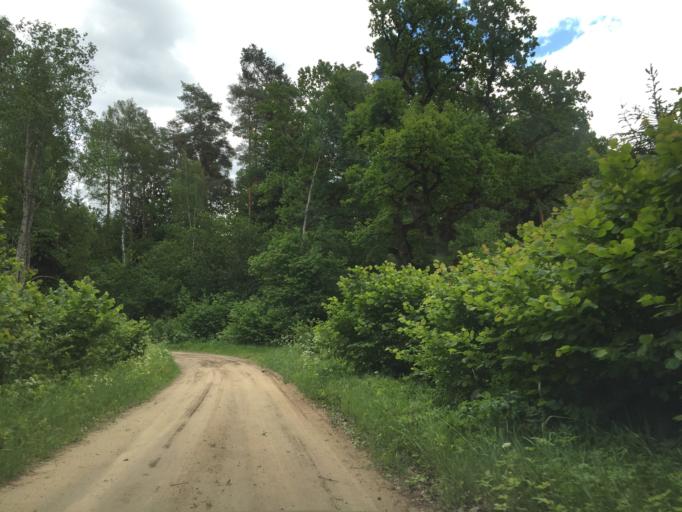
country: LV
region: Lecava
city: Iecava
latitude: 56.5781
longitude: 24.2707
